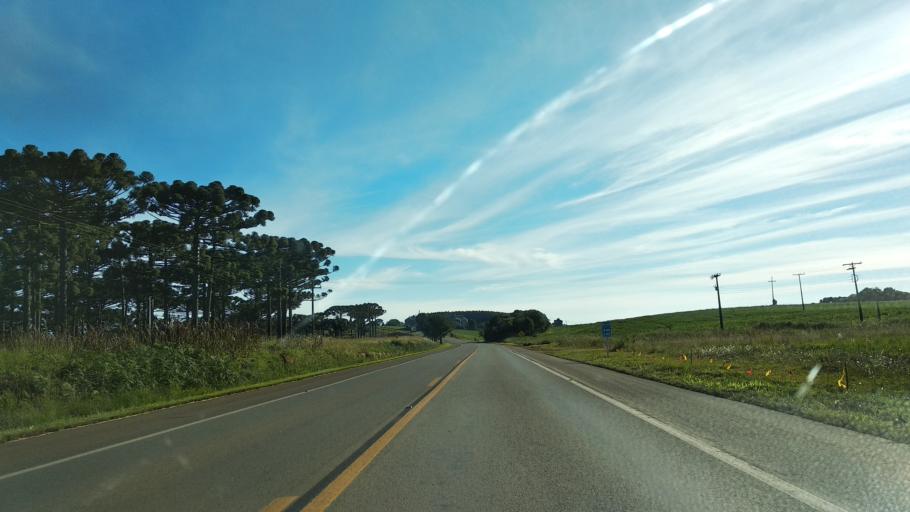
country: BR
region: Santa Catarina
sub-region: Celso Ramos
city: Celso Ramos
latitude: -27.5269
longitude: -51.3716
